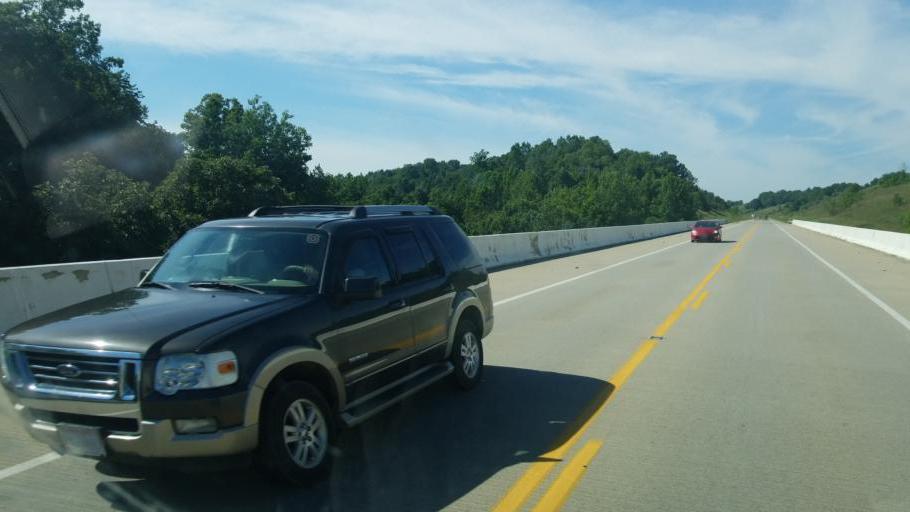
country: US
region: Ohio
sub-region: Athens County
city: Athens
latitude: 39.2191
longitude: -82.0650
